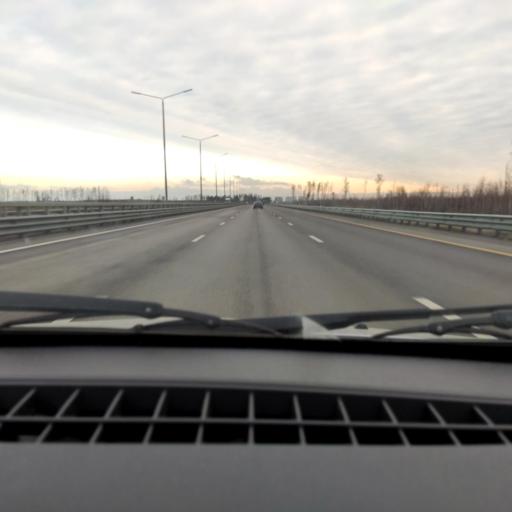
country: RU
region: Voronezj
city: Somovo
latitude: 51.7680
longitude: 39.3042
